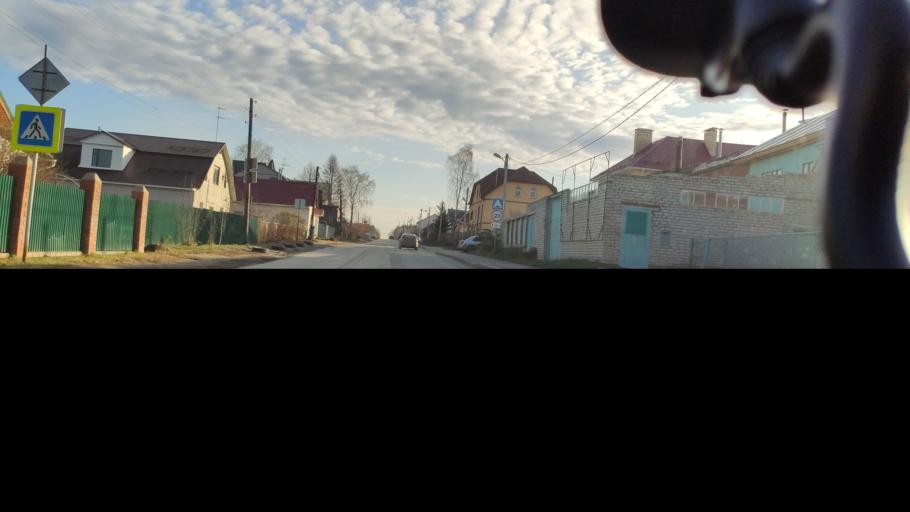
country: RU
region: Perm
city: Kondratovo
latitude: 58.0461
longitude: 56.0464
